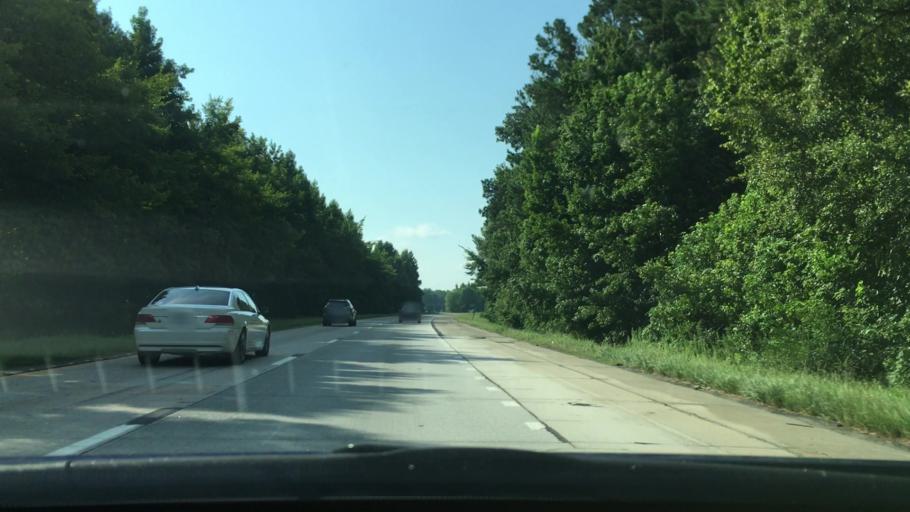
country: US
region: South Carolina
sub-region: Orangeburg County
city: Holly Hill
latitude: 33.2648
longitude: -80.4813
